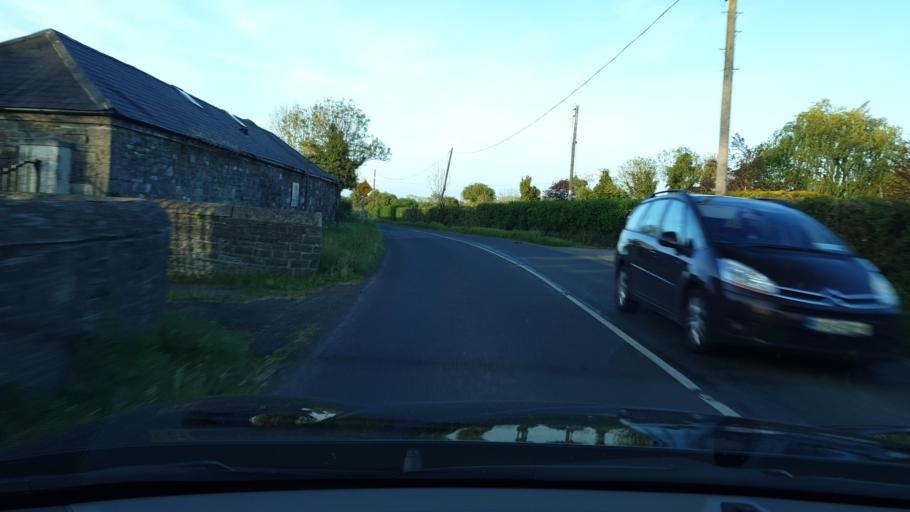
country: IE
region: Leinster
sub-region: An Mhi
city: Ashbourne
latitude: 53.5099
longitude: -6.4297
